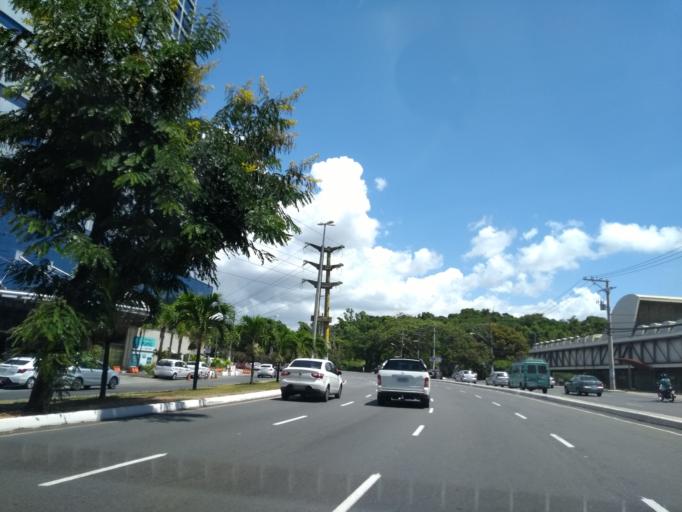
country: BR
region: Bahia
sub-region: Salvador
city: Salvador
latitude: -12.9812
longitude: -38.4501
